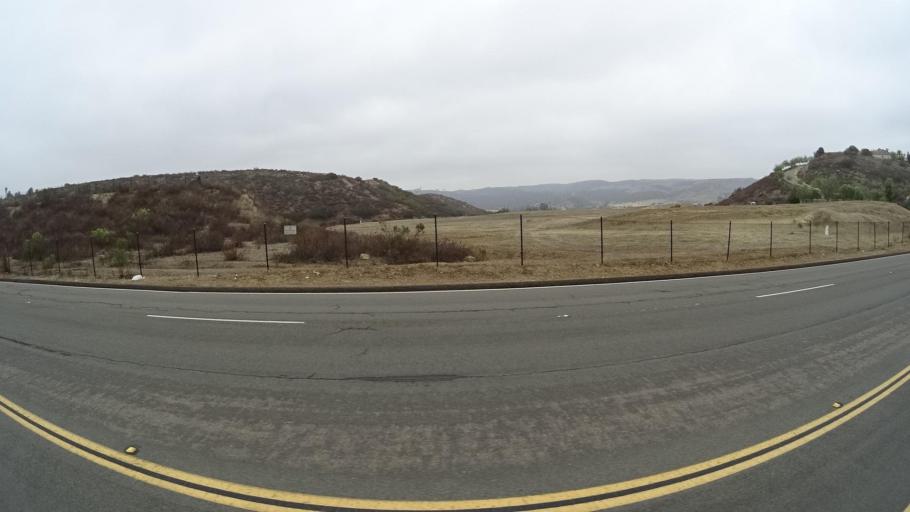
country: US
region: California
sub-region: San Diego County
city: Poway
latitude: 32.9675
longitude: -117.0197
